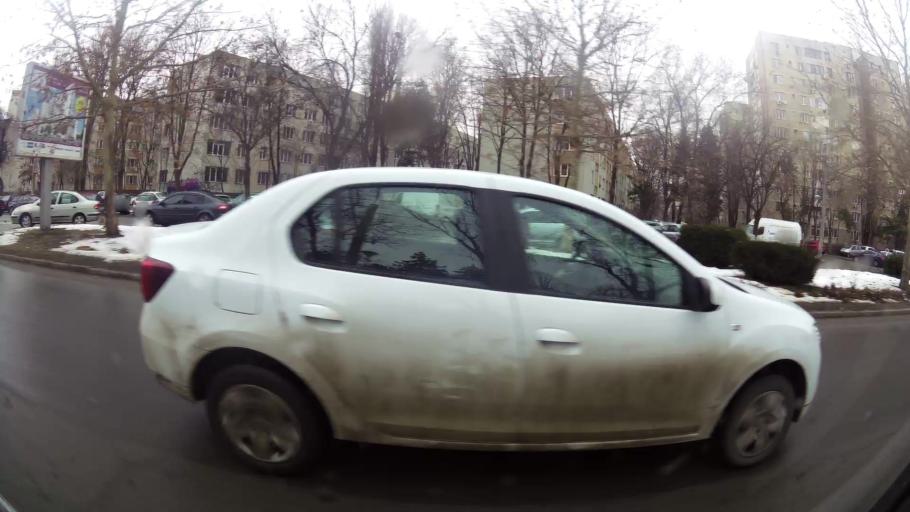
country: RO
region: Ilfov
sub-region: Comuna Chiajna
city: Rosu
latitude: 44.4181
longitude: 26.0287
